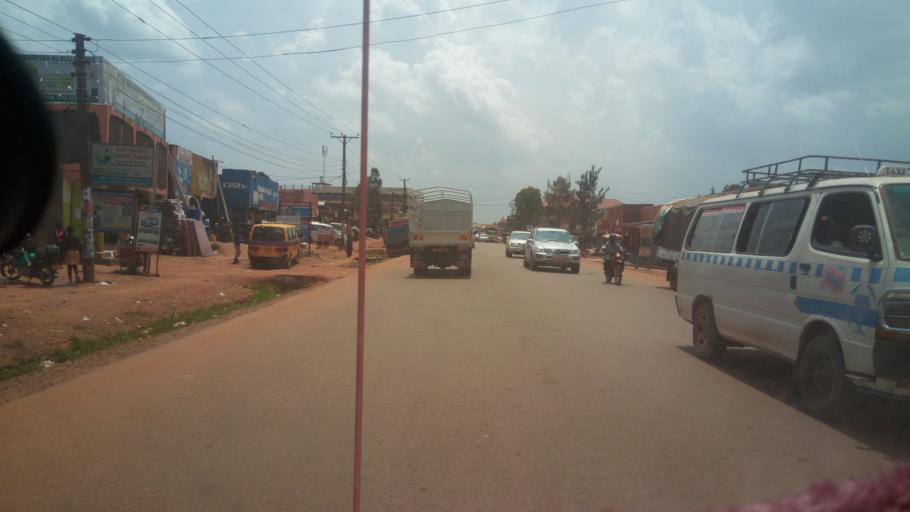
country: UG
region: Central Region
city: Kampala Central Division
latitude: 0.3656
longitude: 32.5261
